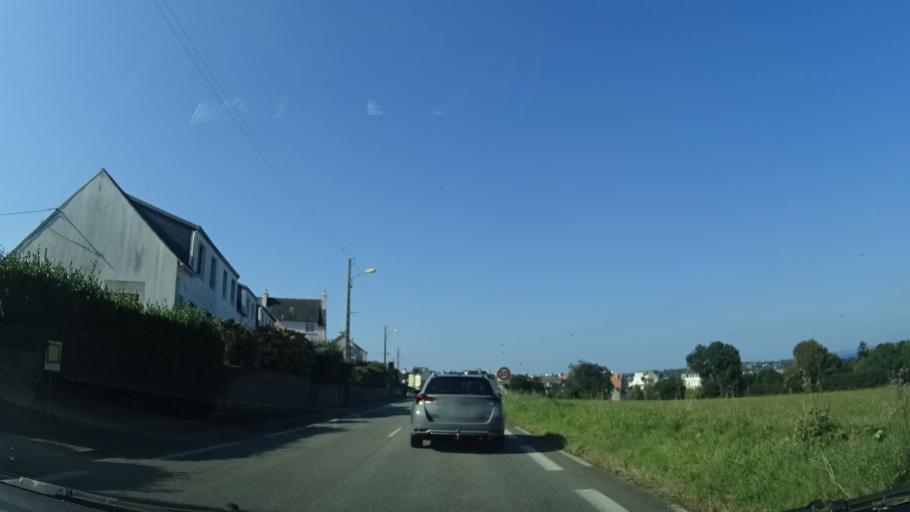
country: FR
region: Brittany
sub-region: Departement du Finistere
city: Douarnenez
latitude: 48.0877
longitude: -4.3180
